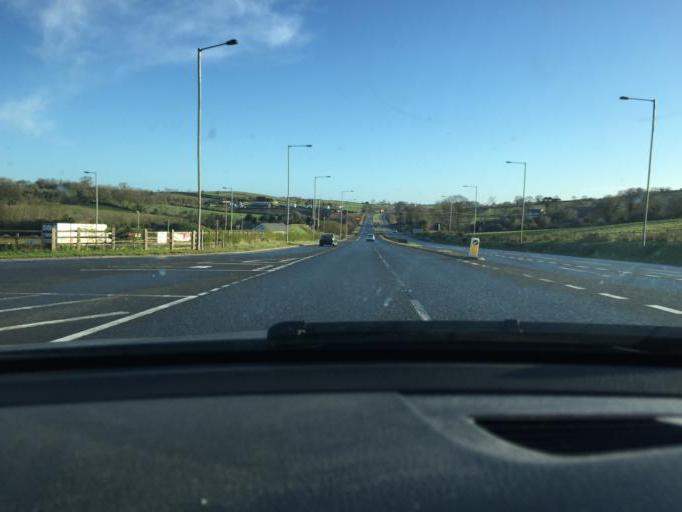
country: GB
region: Northern Ireland
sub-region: Banbridge District
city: Banbridge
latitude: 54.3193
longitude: -6.2994
